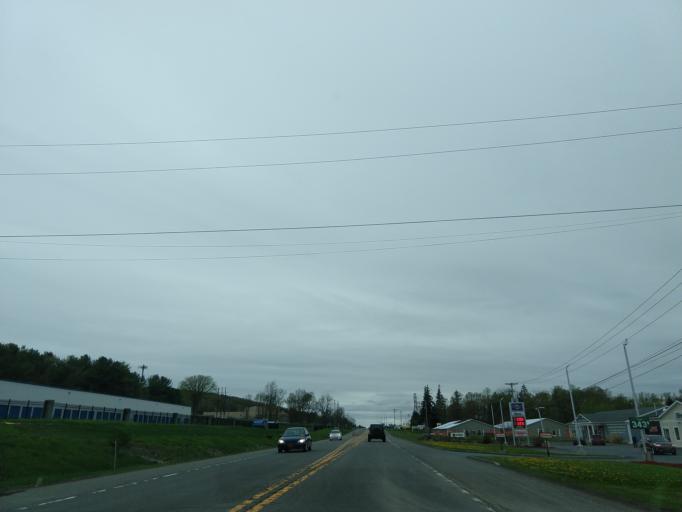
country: US
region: New York
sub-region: Tompkins County
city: Northeast Ithaca
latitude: 42.4719
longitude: -76.3998
